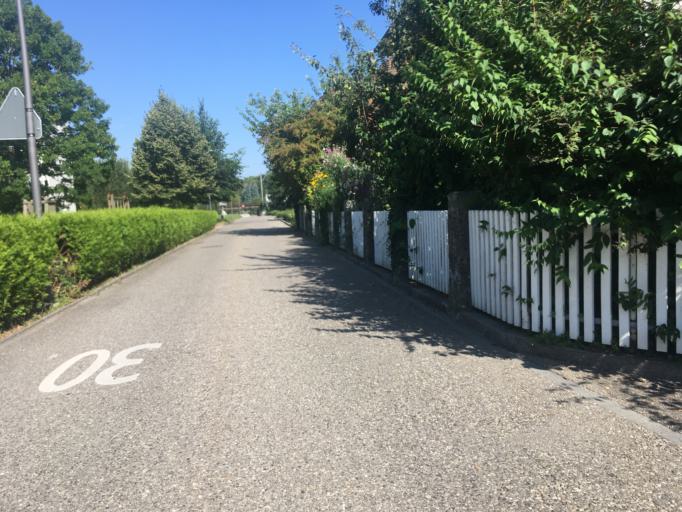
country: CH
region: Bern
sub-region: Emmental District
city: Burgdorf
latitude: 47.0597
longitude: 7.6296
